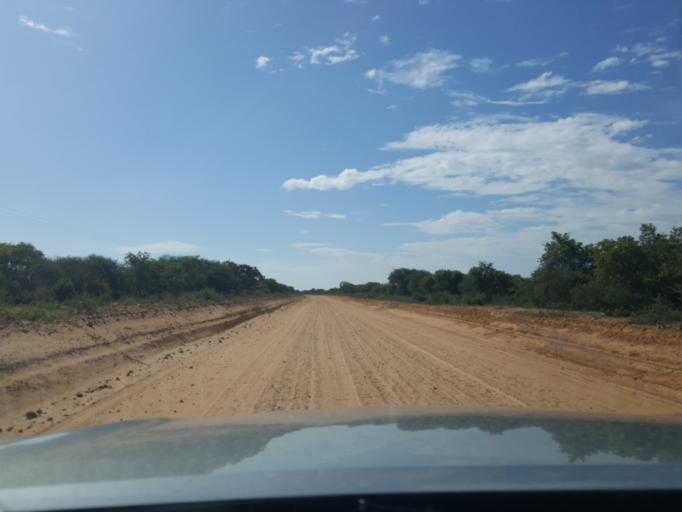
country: BW
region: Kweneng
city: Khudumelapye
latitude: -23.7293
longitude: 24.7430
